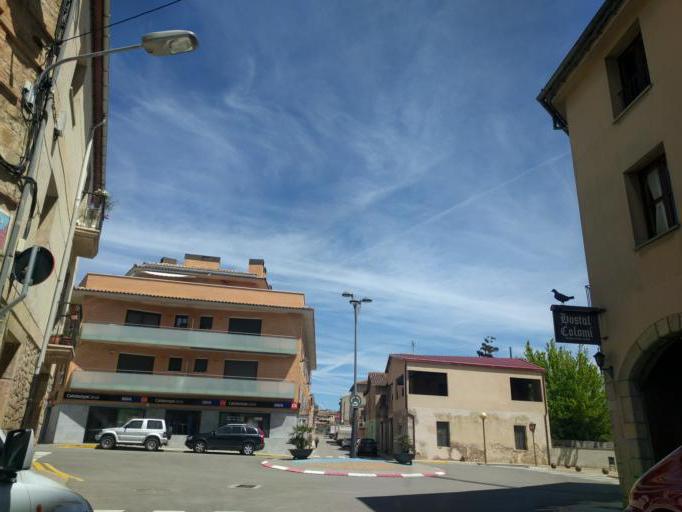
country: ES
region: Catalonia
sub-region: Provincia de Tarragona
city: Santa Coloma de Queralt
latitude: 41.5334
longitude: 1.3833
